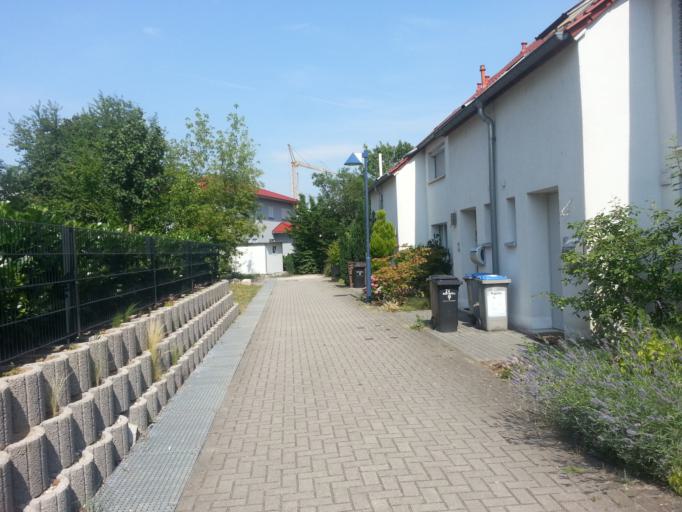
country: DE
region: Baden-Wuerttemberg
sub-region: Karlsruhe Region
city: Ilvesheim
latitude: 49.5013
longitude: 8.5453
